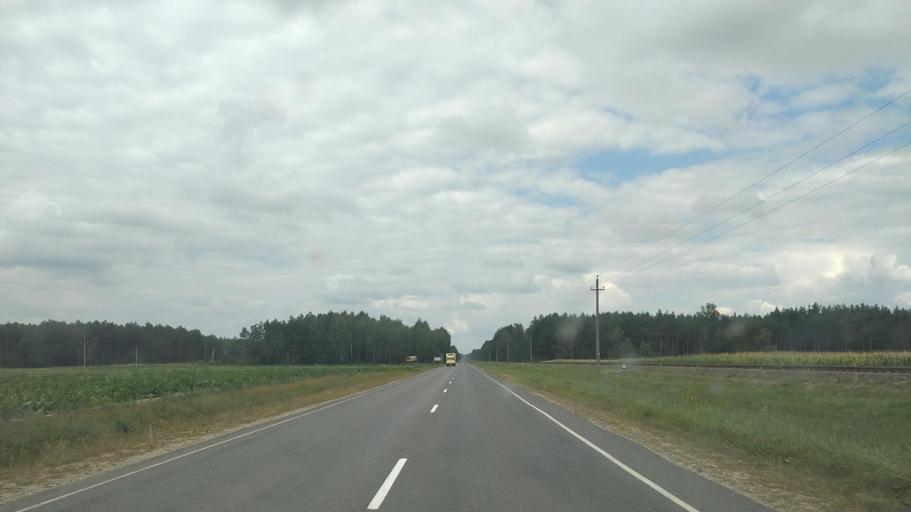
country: BY
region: Brest
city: Byelaazyorsk
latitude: 52.5198
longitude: 25.1511
